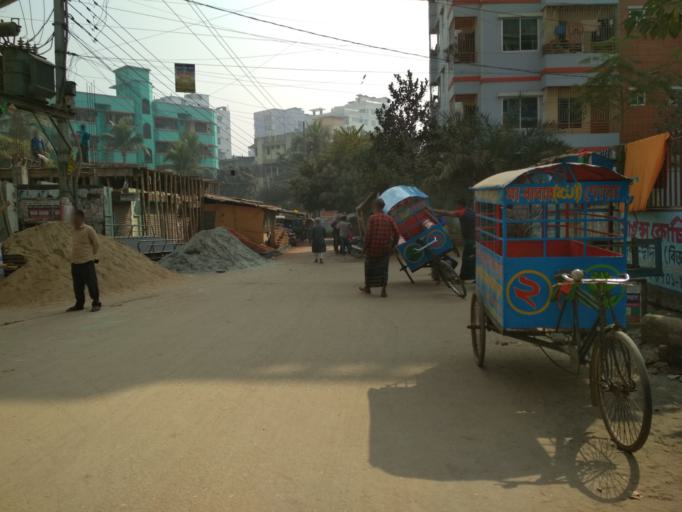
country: BD
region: Dhaka
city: Azimpur
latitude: 23.8093
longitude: 90.3747
